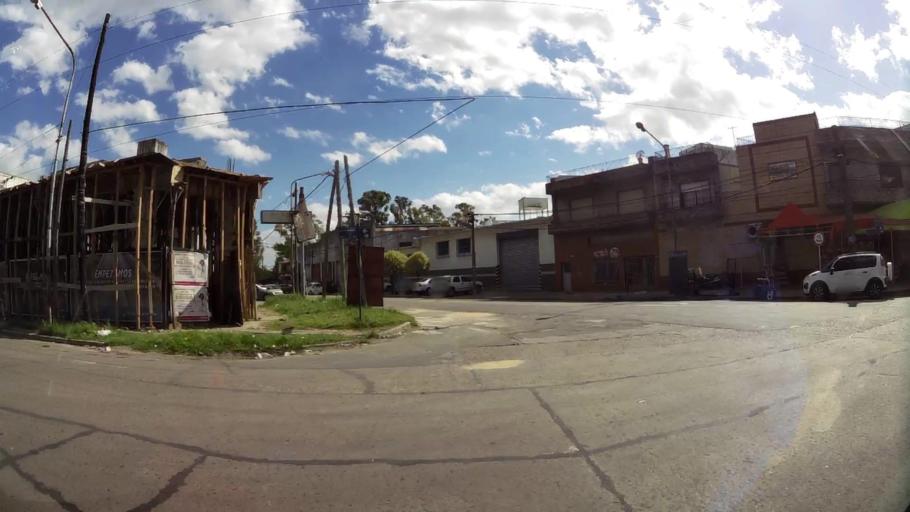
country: AR
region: Buenos Aires
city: San Justo
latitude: -34.6527
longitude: -58.5519
